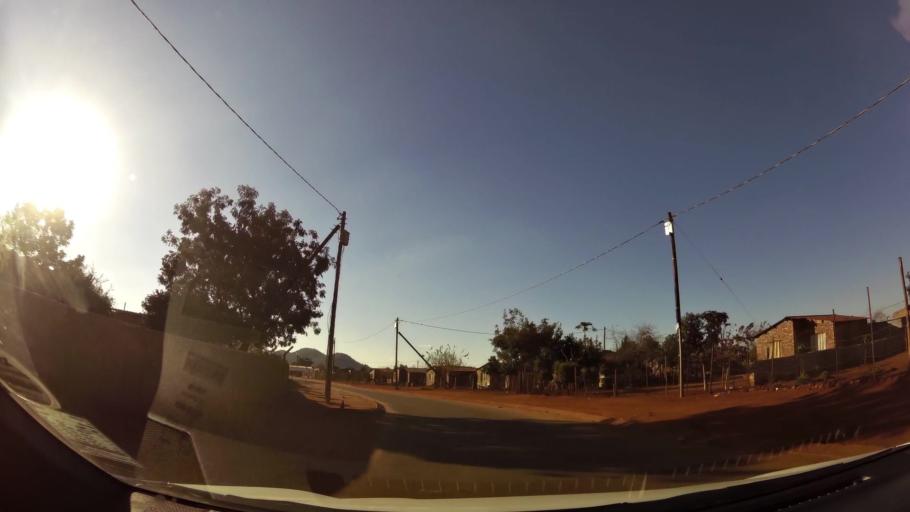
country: ZA
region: Limpopo
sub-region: Waterberg District Municipality
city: Mokopane
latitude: -24.1800
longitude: 28.9777
